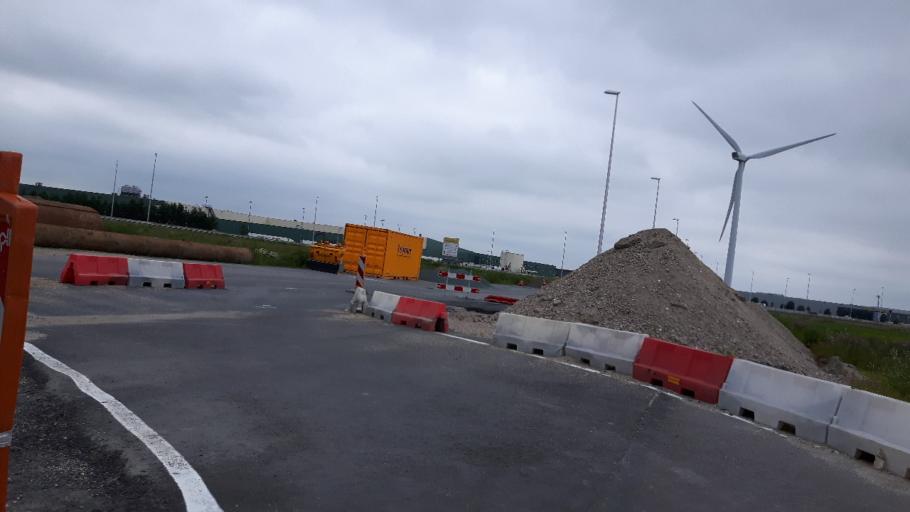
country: NL
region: South Holland
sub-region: Gemeente Waddinxveen
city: Waddinxveen
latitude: 52.0218
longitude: 4.6399
